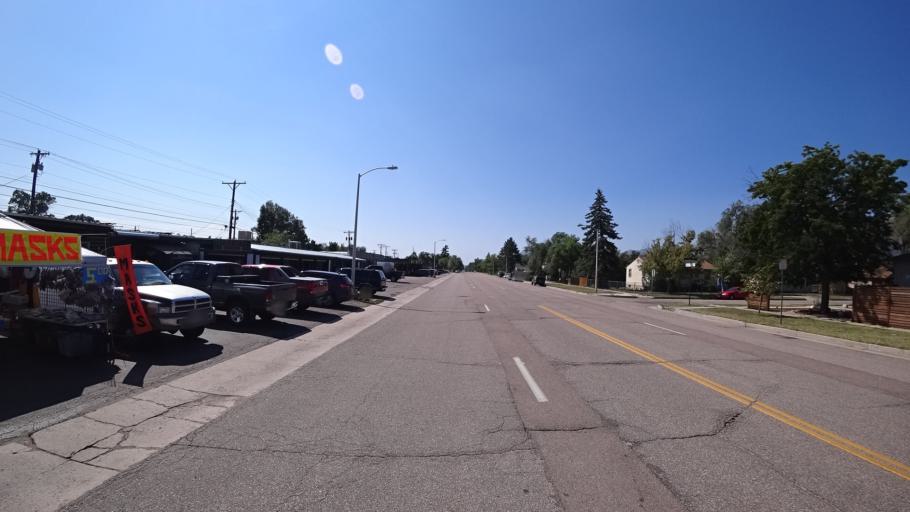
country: US
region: Colorado
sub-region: El Paso County
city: Colorado Springs
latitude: 38.8658
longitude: -104.8181
